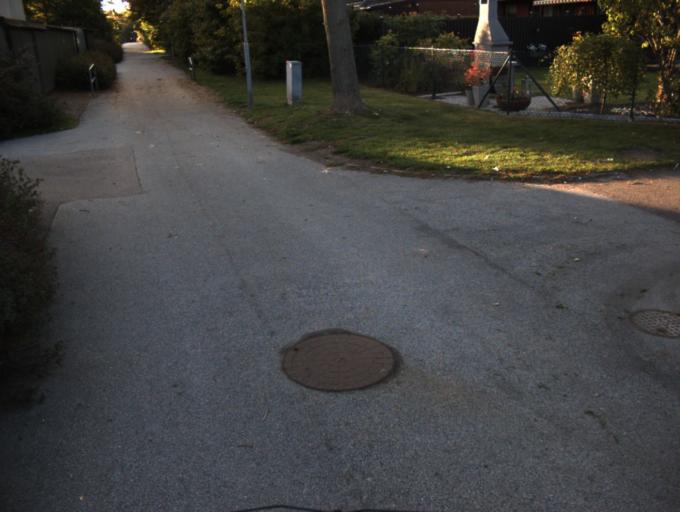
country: SE
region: Skane
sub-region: Helsingborg
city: Rydeback
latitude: 56.0145
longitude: 12.7602
